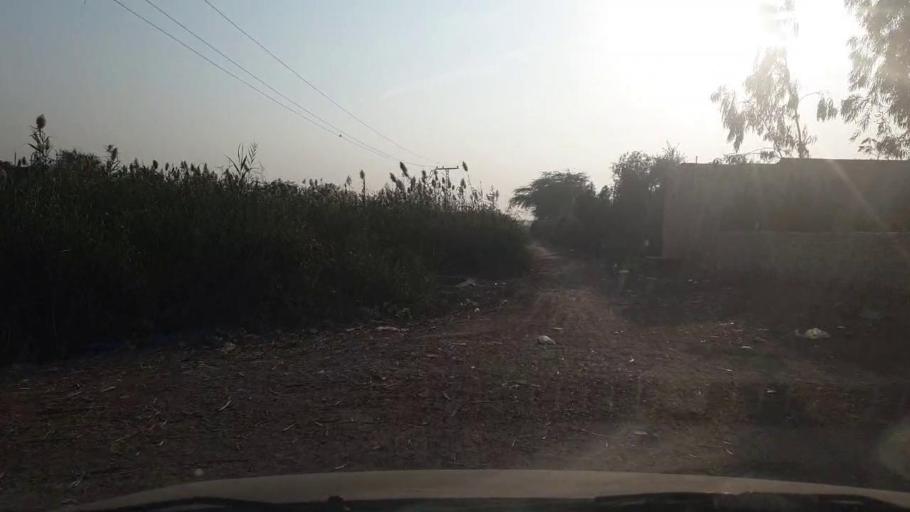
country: PK
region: Sindh
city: Mirwah Gorchani
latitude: 25.3725
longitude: 69.1248
